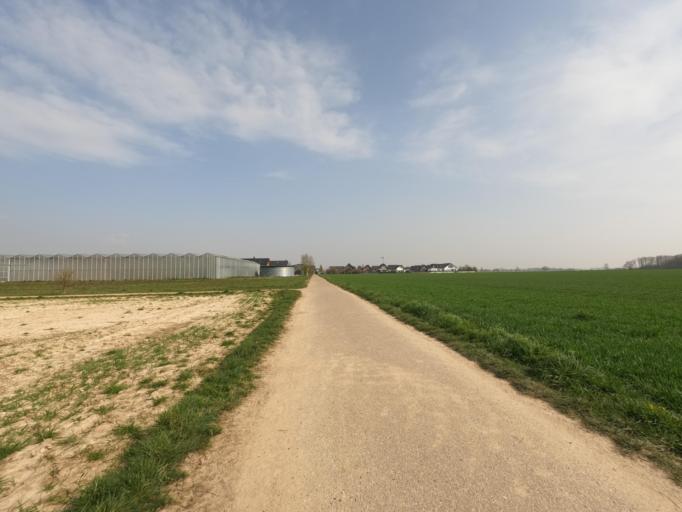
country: DE
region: North Rhine-Westphalia
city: Erkelenz
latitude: 51.0578
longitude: 6.3303
